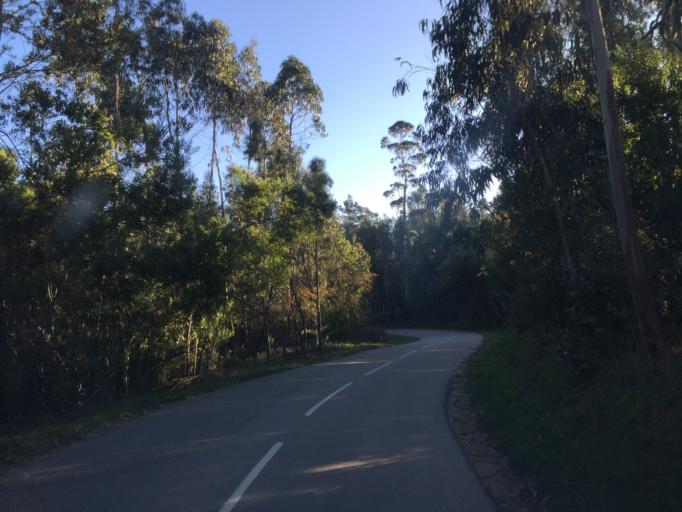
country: PT
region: Coimbra
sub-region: Figueira da Foz
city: Alhadas
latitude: 40.1585
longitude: -8.8006
